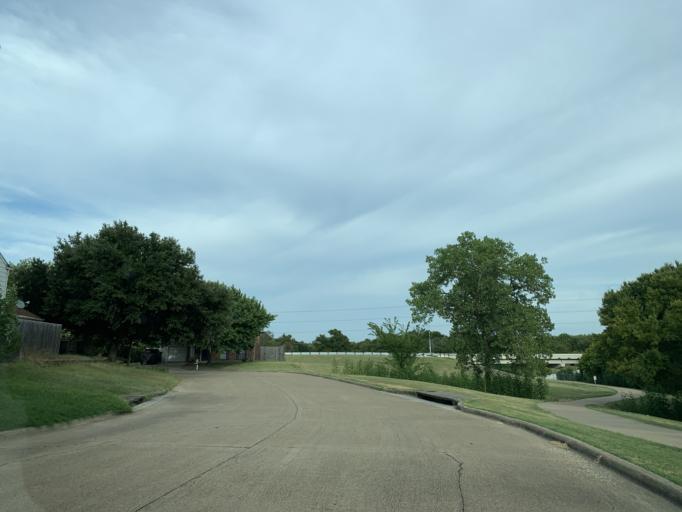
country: US
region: Texas
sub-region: Dallas County
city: Grand Prairie
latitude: 32.6600
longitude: -97.0434
